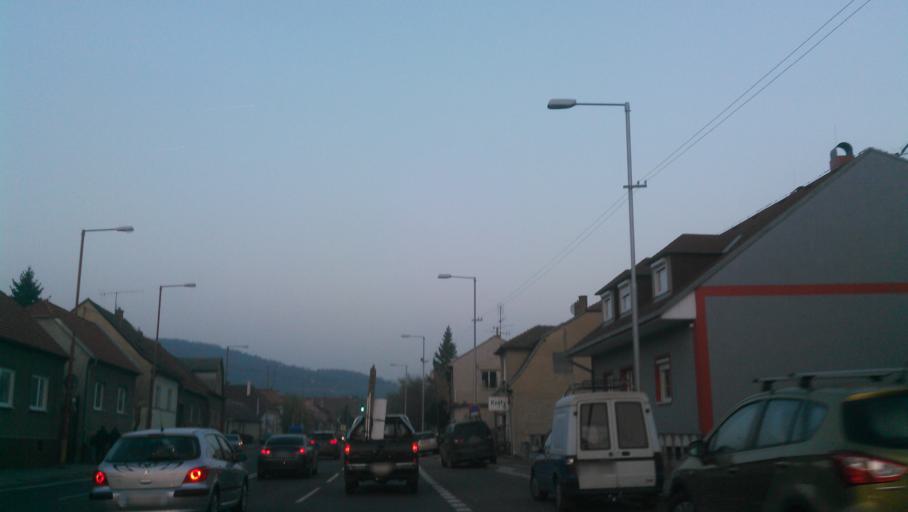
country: SK
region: Bratislavsky
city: Svaty Jur
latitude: 48.2498
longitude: 17.2134
